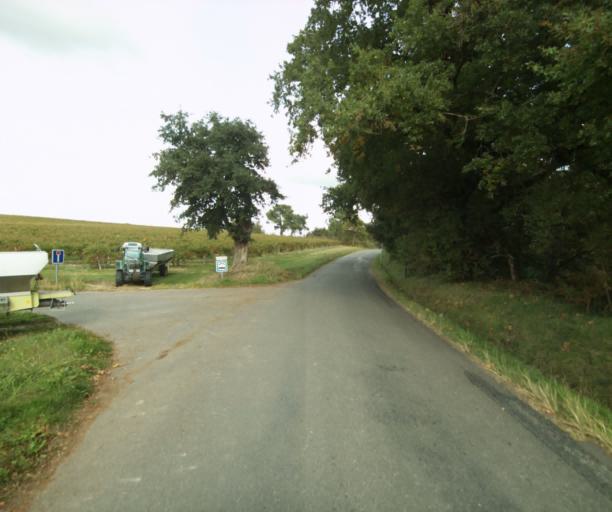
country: FR
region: Midi-Pyrenees
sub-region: Departement du Gers
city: Eauze
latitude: 43.8463
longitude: 0.1544
